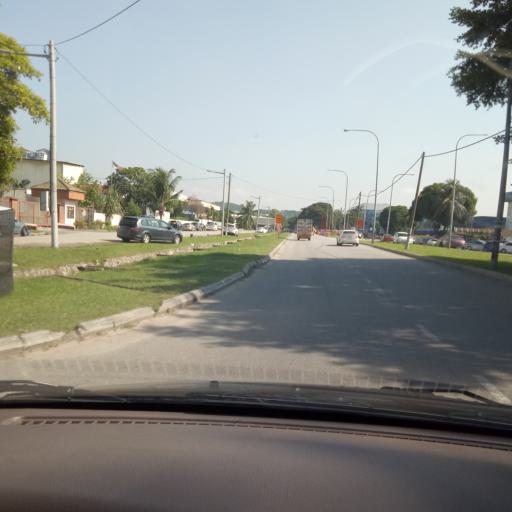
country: MY
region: Selangor
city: Kampong Baharu Balakong
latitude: 3.0228
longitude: 101.7652
